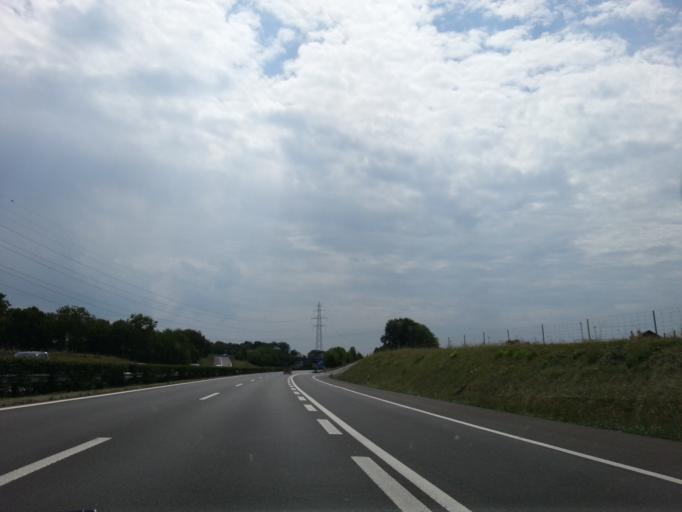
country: CH
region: Vaud
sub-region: Jura-Nord vaudois District
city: Chavornay
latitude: 46.7099
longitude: 6.5793
